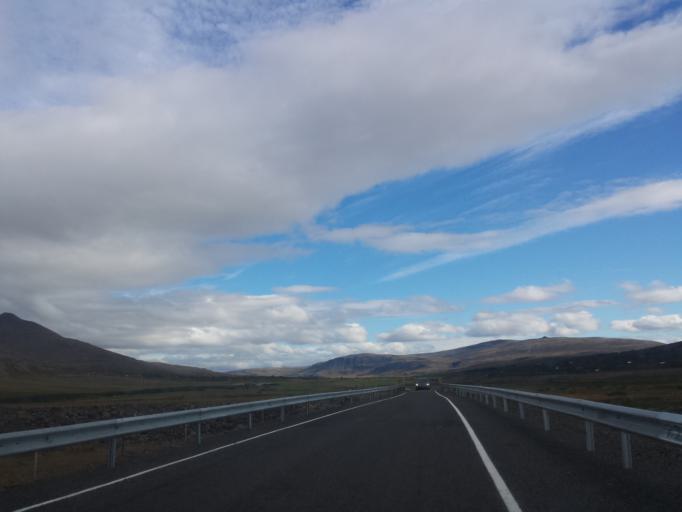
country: IS
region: West
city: Borgarnes
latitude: 64.4276
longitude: -21.6988
